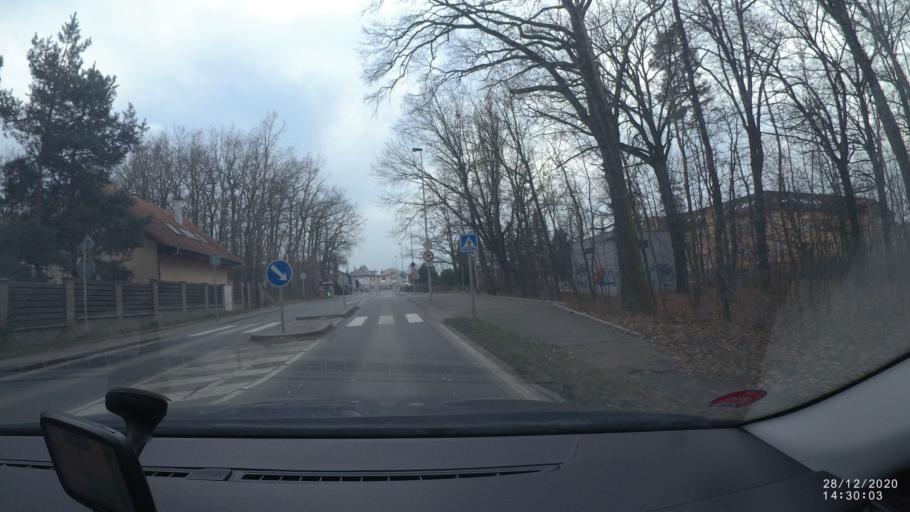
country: CZ
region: Central Bohemia
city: Sestajovice
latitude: 50.0785
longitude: 14.6602
